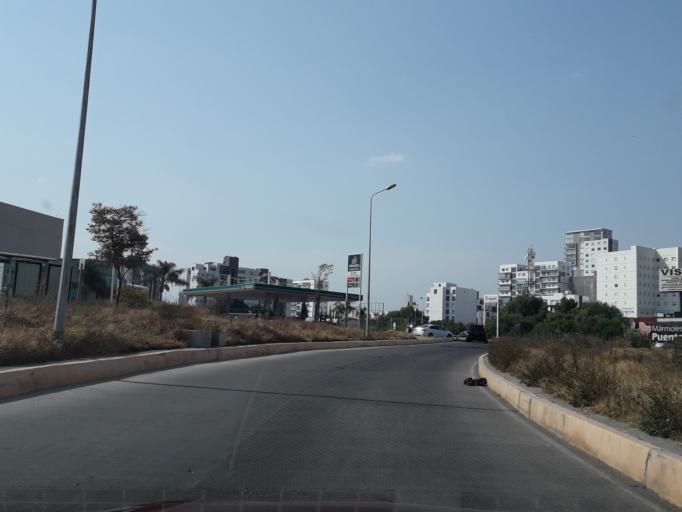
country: MX
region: Puebla
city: Puebla
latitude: 19.0343
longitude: -98.2268
